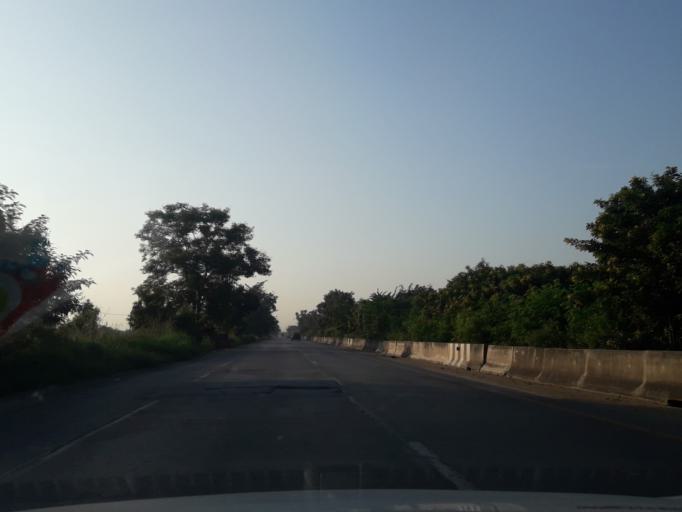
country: TH
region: Phra Nakhon Si Ayutthaya
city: Bang Pa-in
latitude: 14.1803
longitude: 100.5583
